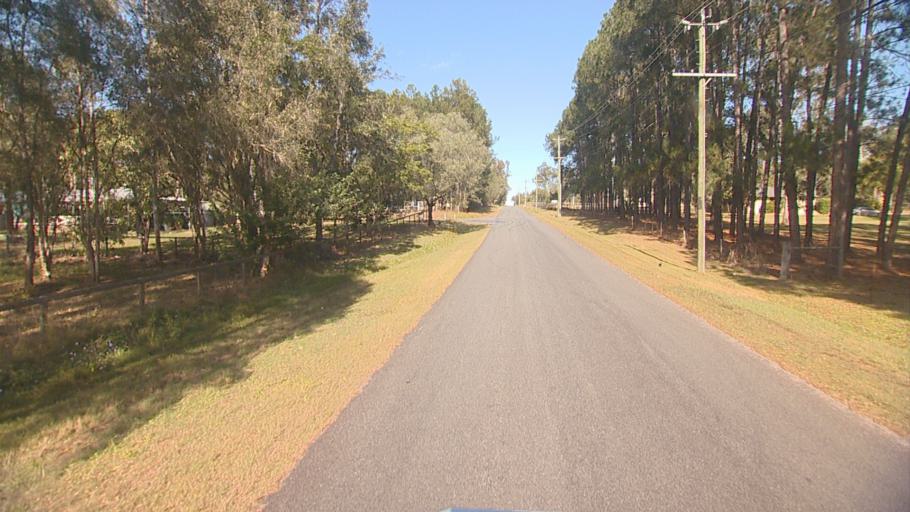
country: AU
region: Queensland
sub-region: Logan
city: North Maclean
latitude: -27.7752
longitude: 152.9914
